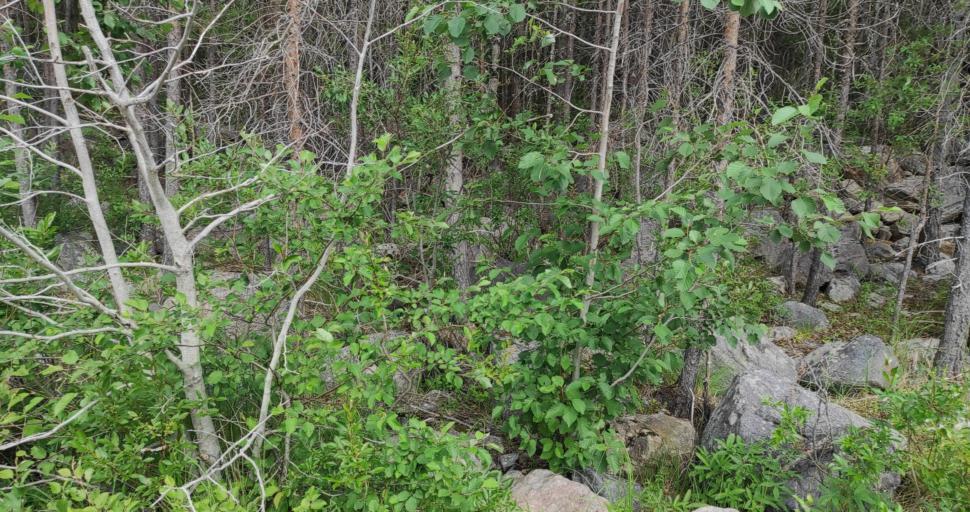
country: RU
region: Murmansk
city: Poyakonda
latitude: 66.7047
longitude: 32.6283
